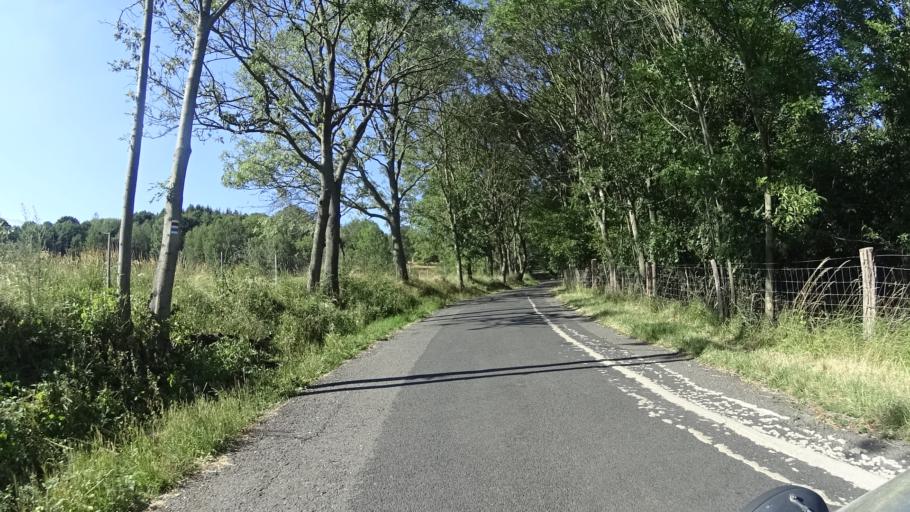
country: CZ
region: Ustecky
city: Zitenice
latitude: 50.5834
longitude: 14.1244
